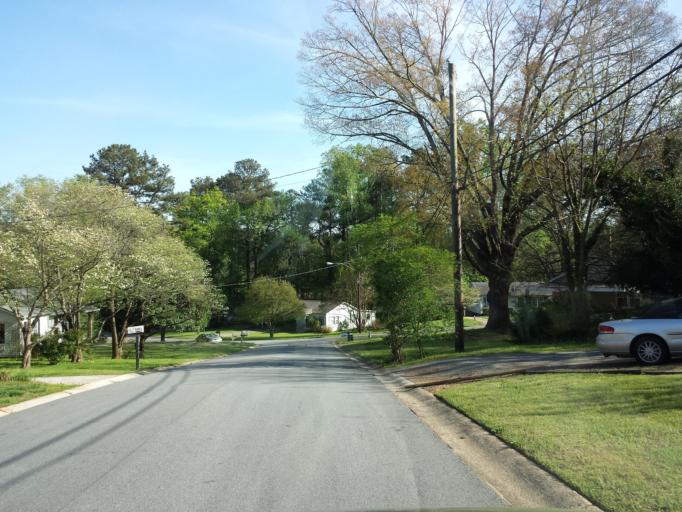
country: US
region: Georgia
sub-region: Cobb County
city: Marietta
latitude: 33.9649
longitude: -84.5181
